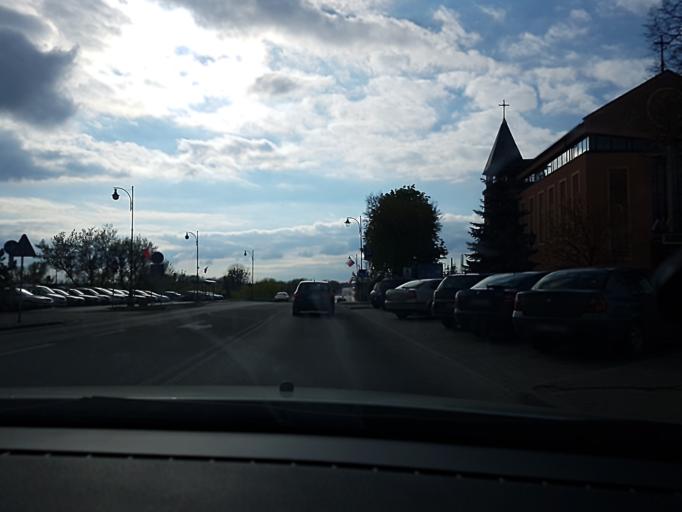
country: PL
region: Masovian Voivodeship
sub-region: Powiat sochaczewski
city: Sochaczew
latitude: 52.2294
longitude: 20.2374
